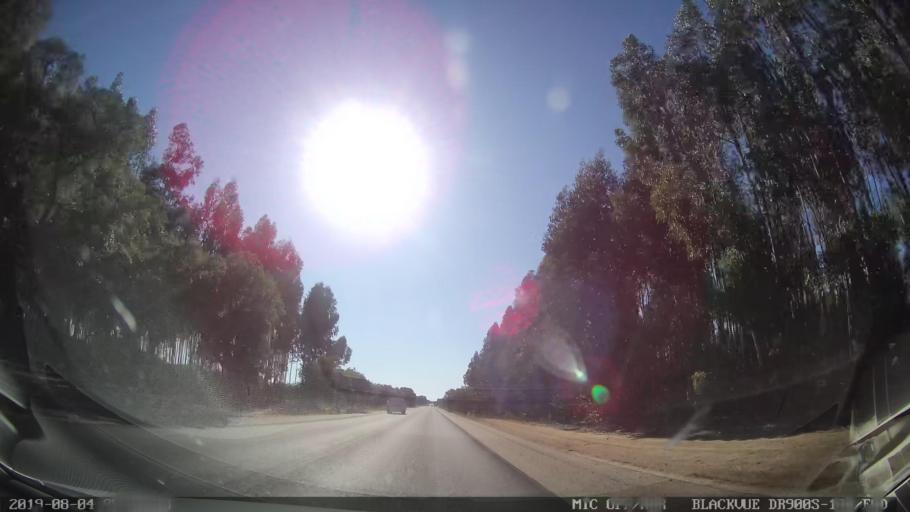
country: PT
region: Portalegre
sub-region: Gaviao
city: Gaviao
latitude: 39.4453
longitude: -7.8816
